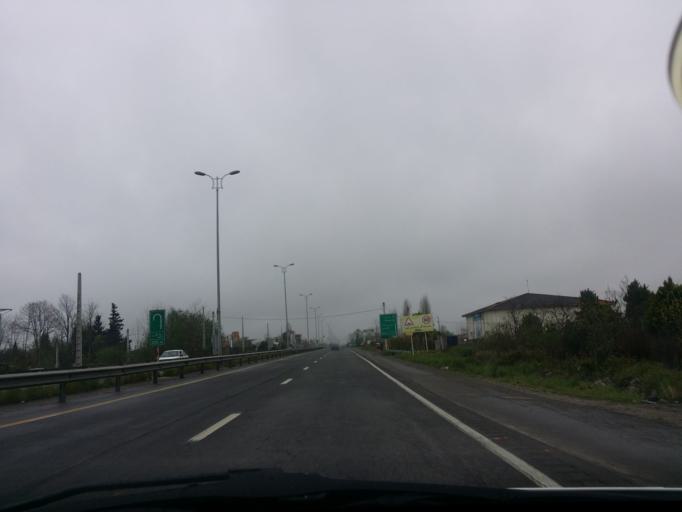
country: IR
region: Mazandaran
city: Tonekabon
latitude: 36.7998
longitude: 50.8908
